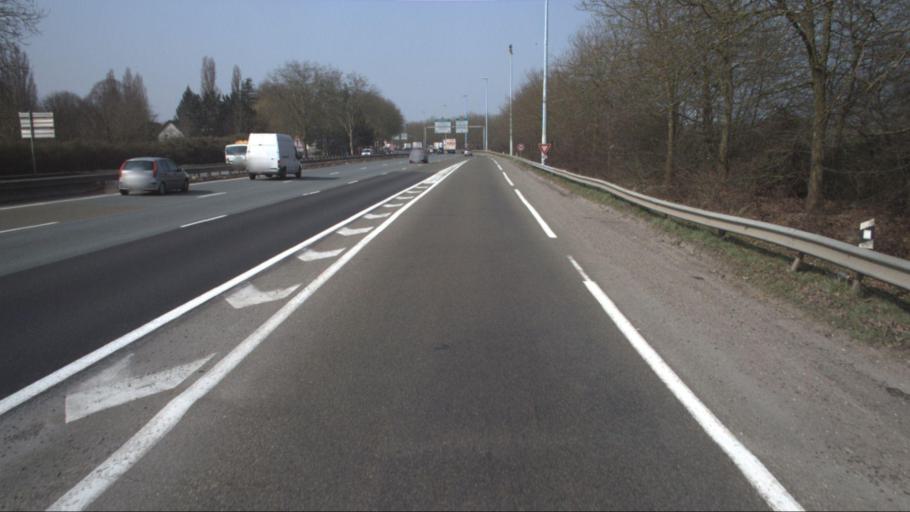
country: FR
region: Ile-de-France
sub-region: Departement des Yvelines
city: Trappes
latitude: 48.7809
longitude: 2.0162
